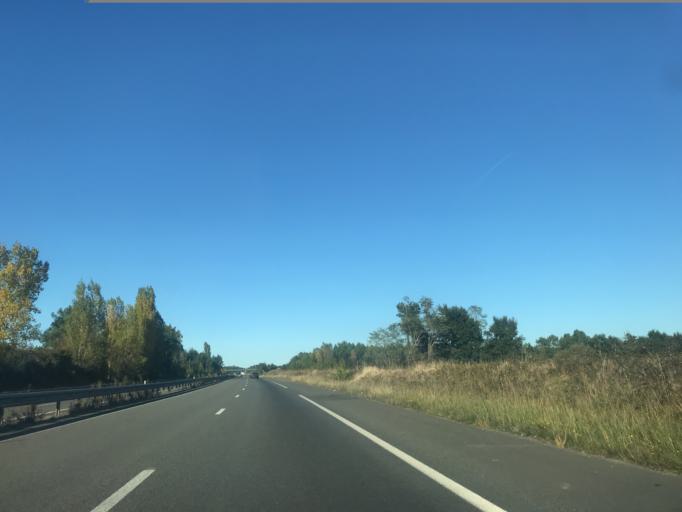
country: FR
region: Poitou-Charentes
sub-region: Departement de la Charente-Maritime
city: Montlieu-la-Garde
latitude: 45.1987
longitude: -0.3053
